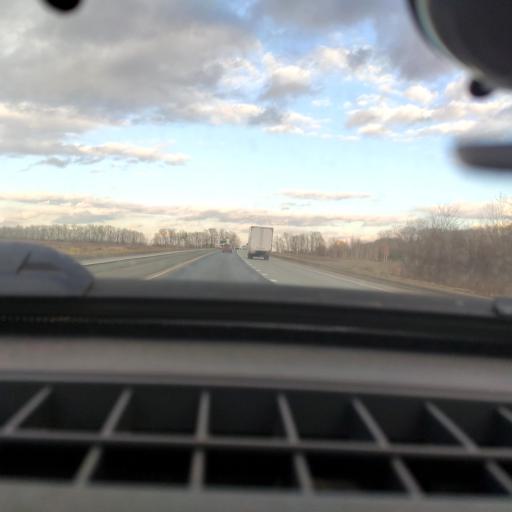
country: RU
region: Bashkortostan
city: Iglino
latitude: 54.7261
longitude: 56.2478
